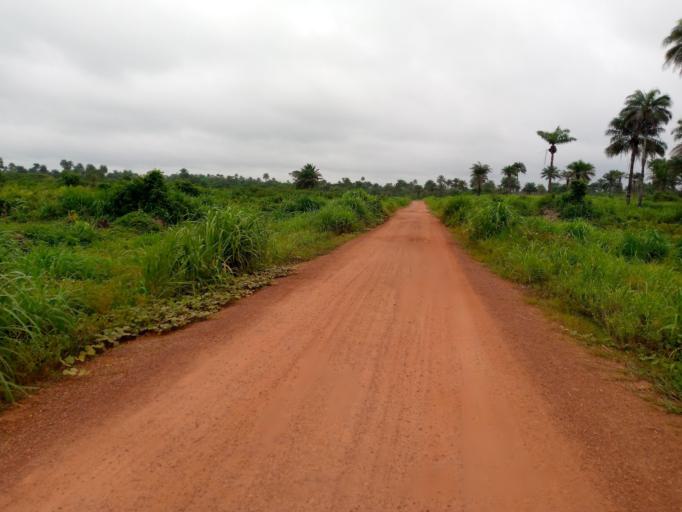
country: SL
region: Southern Province
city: Sumbuya
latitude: 7.5805
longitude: -12.0845
